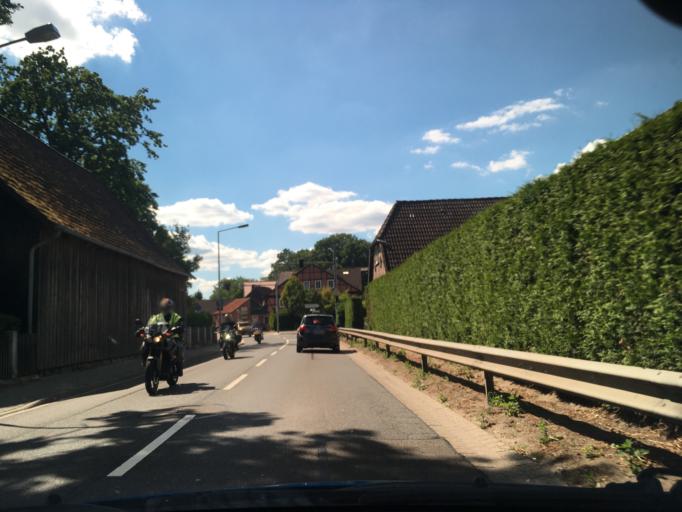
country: DE
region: Lower Saxony
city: Celle
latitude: 52.6050
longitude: 10.1192
